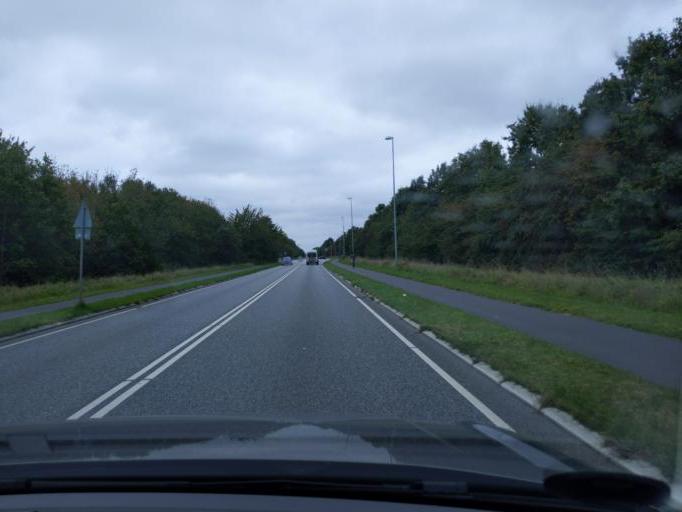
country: DK
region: Central Jutland
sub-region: Randers Kommune
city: Randers
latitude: 56.4818
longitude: 9.9969
